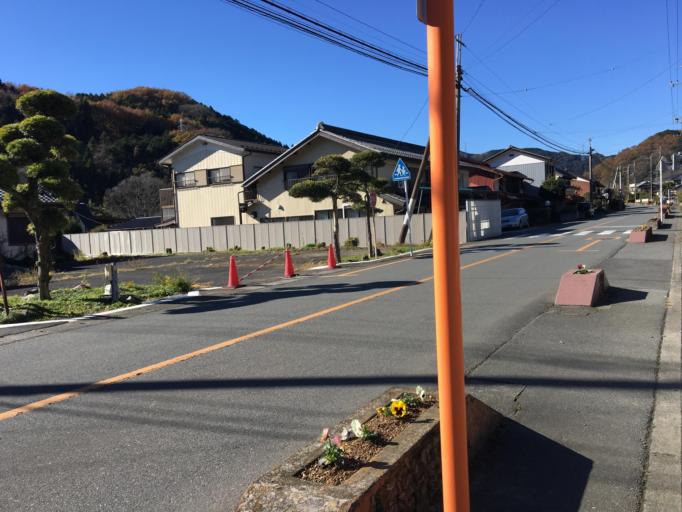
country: JP
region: Saitama
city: Ogawa
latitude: 36.0493
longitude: 139.2266
